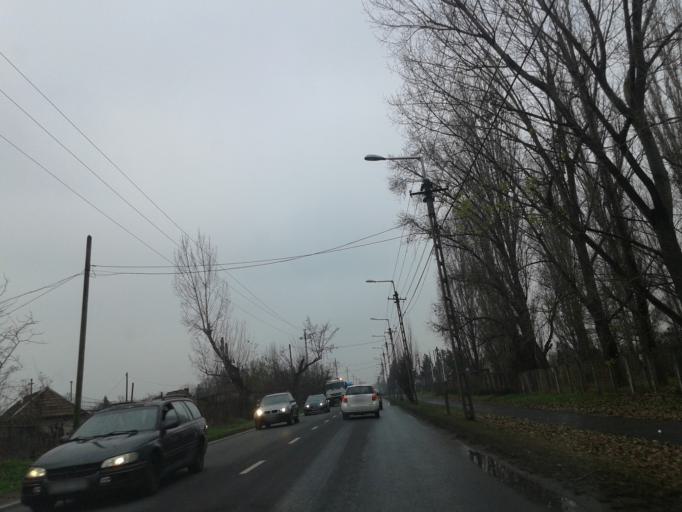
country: HU
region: Budapest
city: Budapest XXII. keruelet
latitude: 47.3974
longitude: 19.0475
